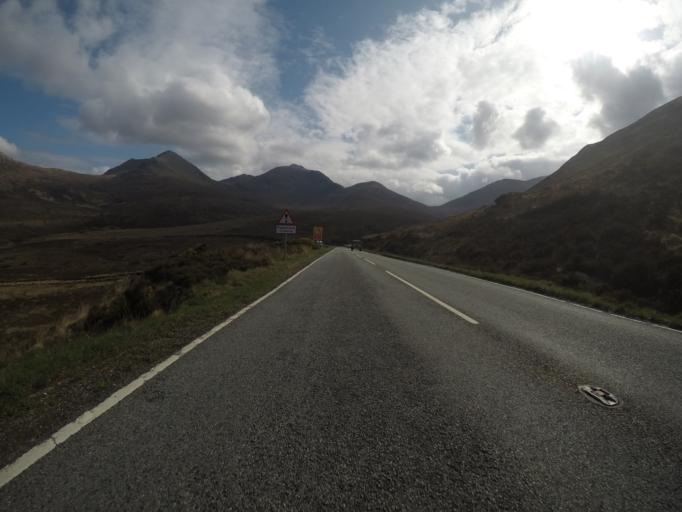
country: GB
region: Scotland
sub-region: Highland
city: Portree
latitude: 57.2661
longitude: -6.0904
